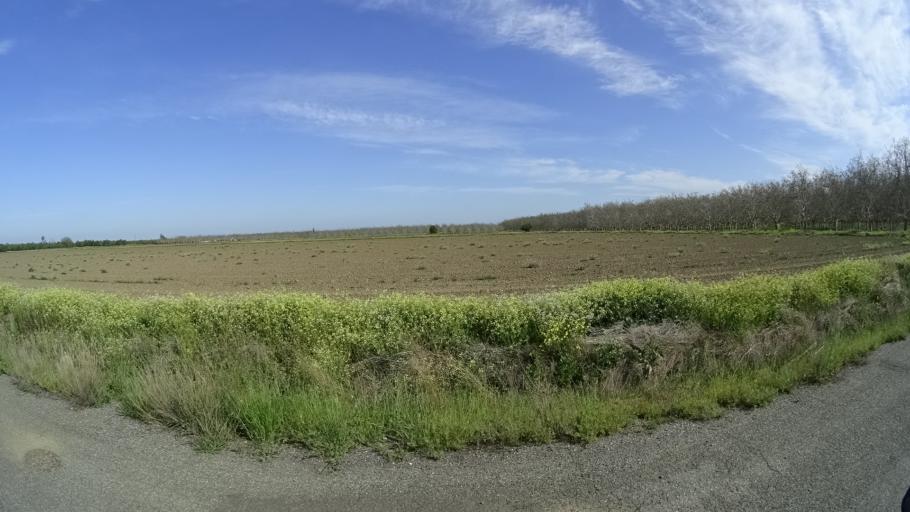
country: US
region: California
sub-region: Glenn County
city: Hamilton City
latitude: 39.6233
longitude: -122.0143
